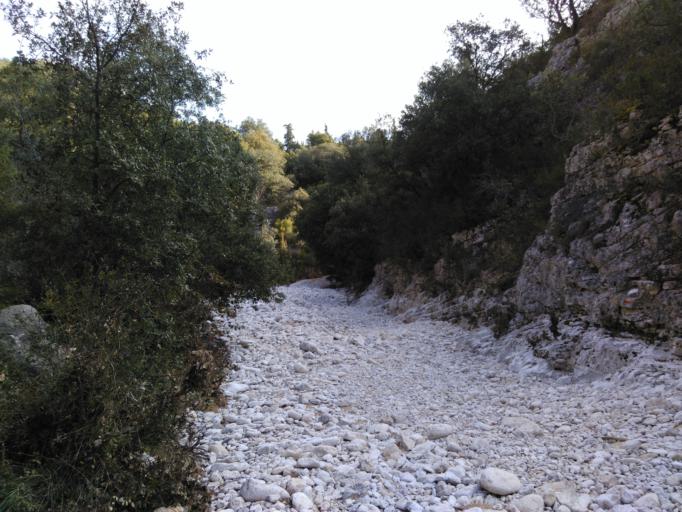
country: FR
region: Provence-Alpes-Cote d'Azur
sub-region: Departement du Vaucluse
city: Villes-sur-Auzon
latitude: 44.0199
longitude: 5.2318
